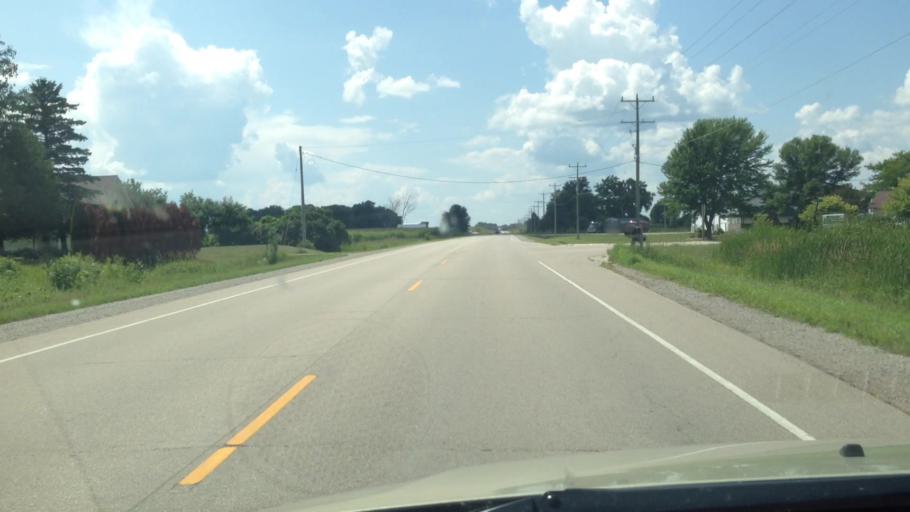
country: US
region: Wisconsin
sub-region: Brown County
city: Pulaski
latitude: 44.6735
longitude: -88.2920
